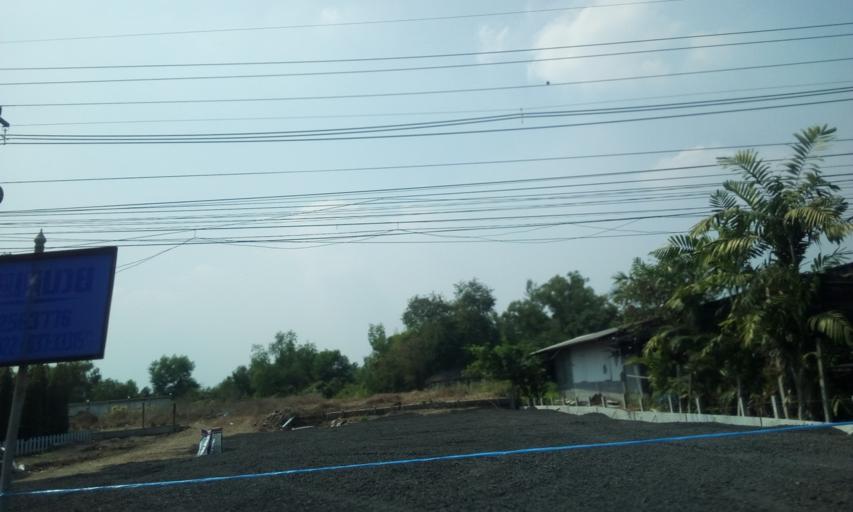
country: TH
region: Nakhon Nayok
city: Ongkharak
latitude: 14.1138
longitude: 100.9434
